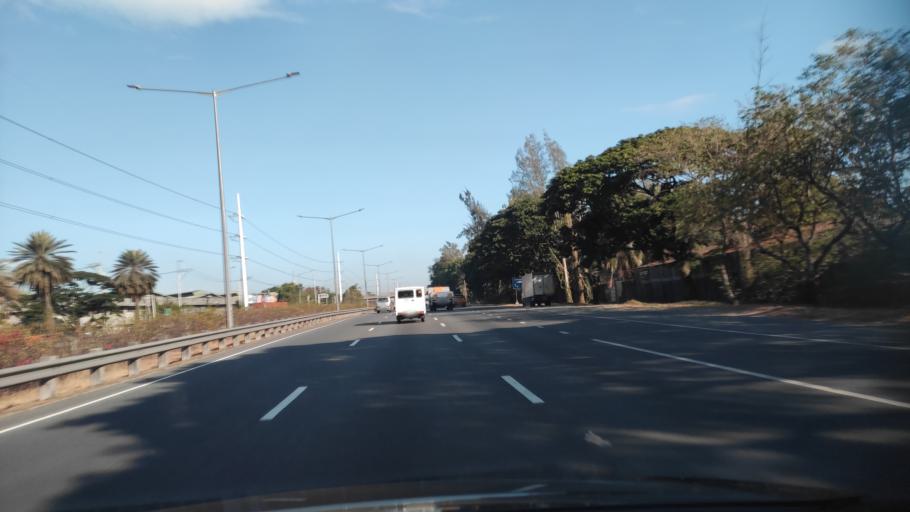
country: PH
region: Central Luzon
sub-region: Province of Bulacan
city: Plaridel
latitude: 14.8626
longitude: 120.8584
